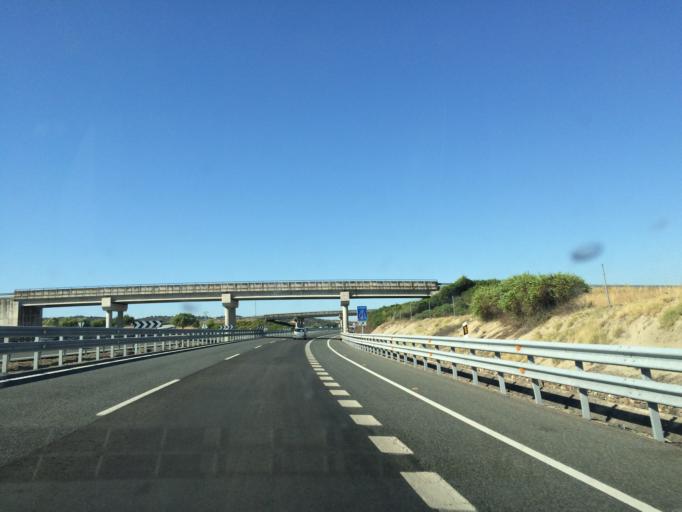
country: ES
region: Castille-La Mancha
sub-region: Province of Toledo
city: Lagartera
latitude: 39.9114
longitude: -5.2110
